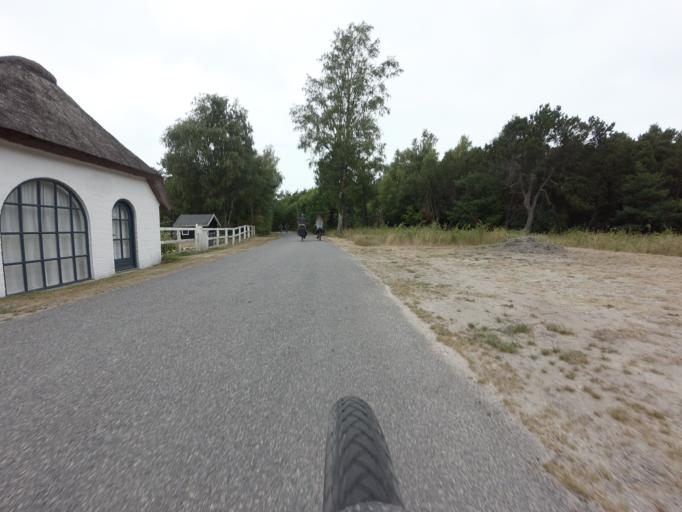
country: DK
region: North Denmark
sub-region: Laeso Kommune
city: Byrum
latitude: 57.2835
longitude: 10.9497
